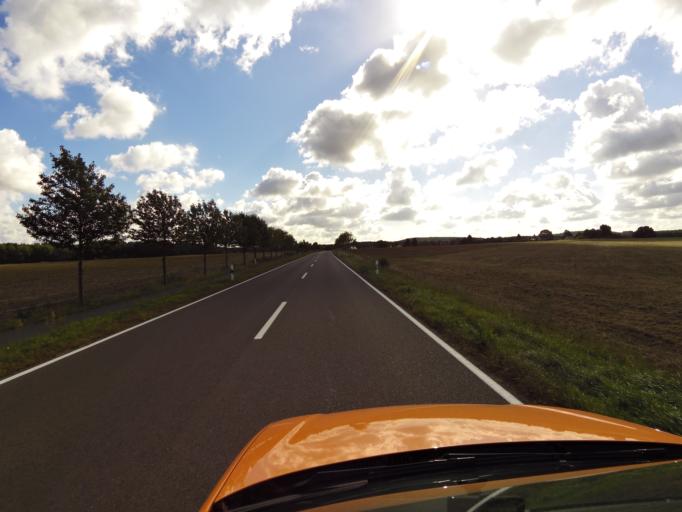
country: DE
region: Brandenburg
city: Michendorf
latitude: 52.2889
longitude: 13.0562
